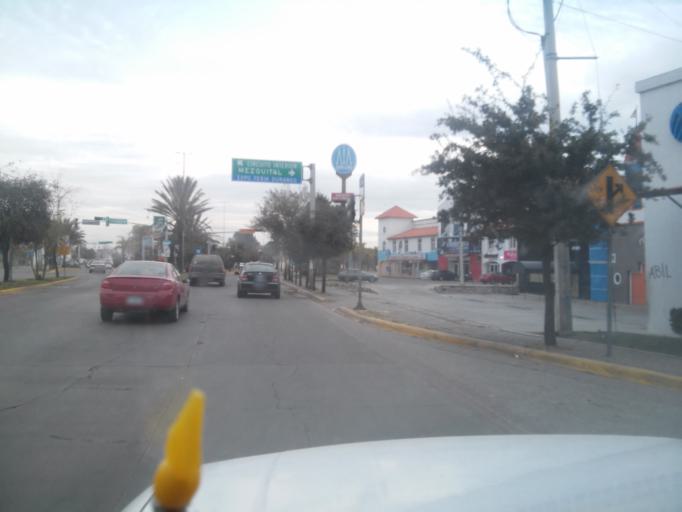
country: MX
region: Durango
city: Victoria de Durango
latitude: 24.0026
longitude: -104.6517
